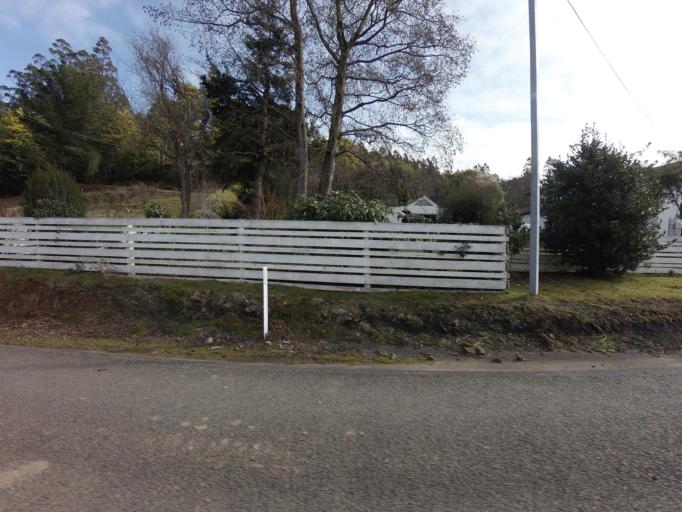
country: AU
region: Tasmania
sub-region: Kingborough
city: Margate
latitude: -43.0208
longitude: 147.1640
